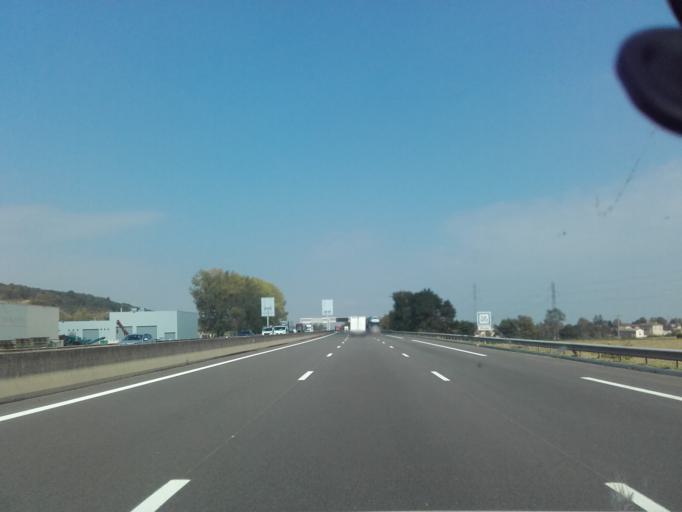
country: FR
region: Bourgogne
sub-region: Departement de Saone-et-Loire
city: Saint-Martin-Belle-Roche
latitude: 46.3834
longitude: 4.8491
